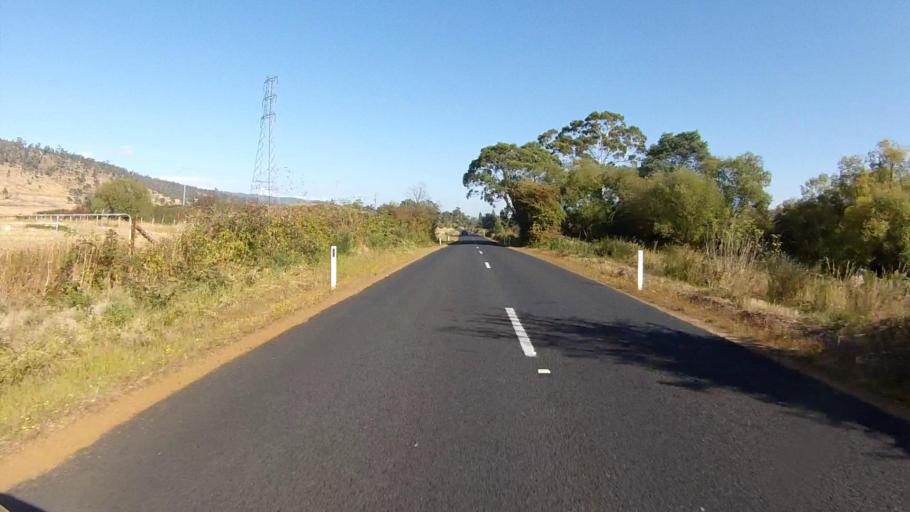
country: AU
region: Tasmania
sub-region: Derwent Valley
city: New Norfolk
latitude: -42.7670
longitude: 147.0211
